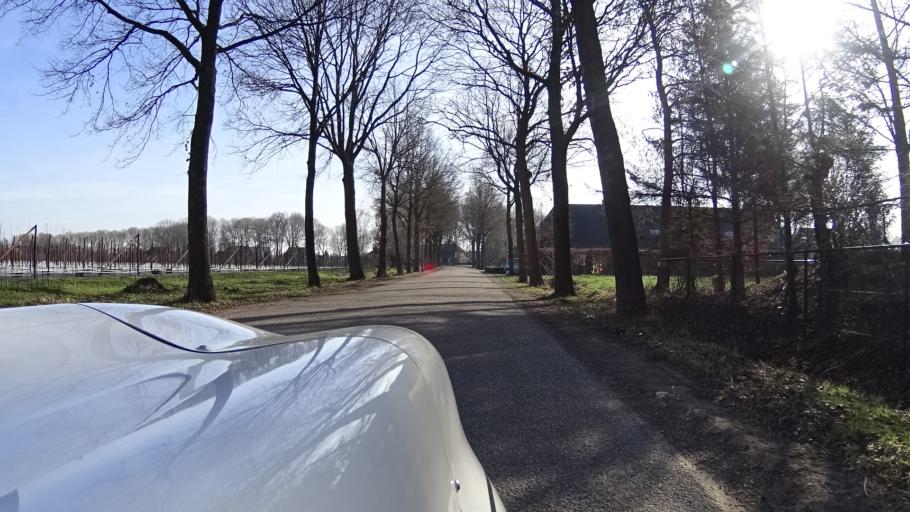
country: NL
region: North Brabant
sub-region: Gemeente Veghel
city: Erp
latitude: 51.6098
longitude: 5.6014
